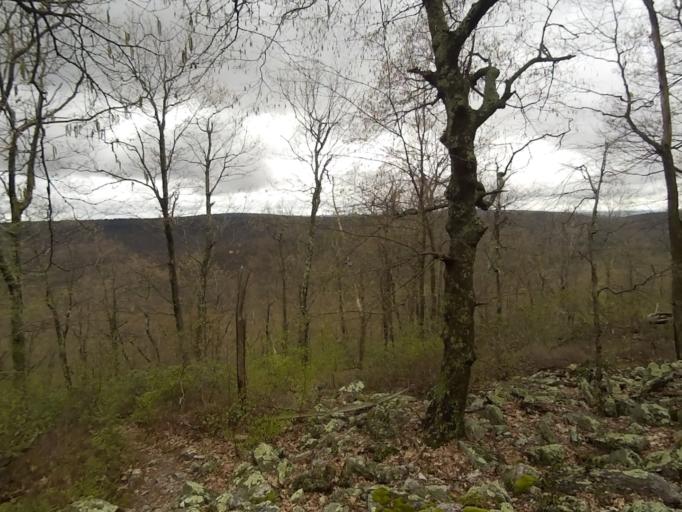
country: US
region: Pennsylvania
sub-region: Centre County
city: Boalsburg
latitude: 40.7483
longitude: -77.7547
